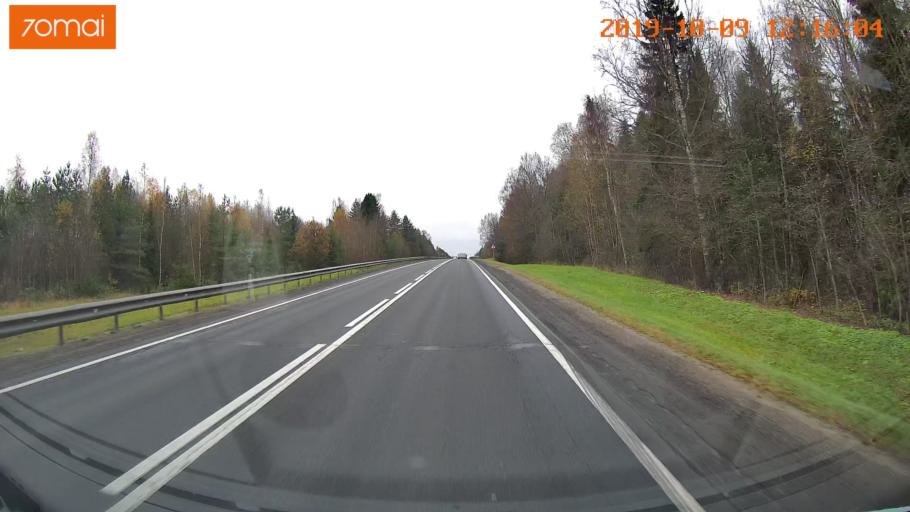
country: RU
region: Jaroslavl
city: Prechistoye
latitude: 58.4741
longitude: 40.3217
